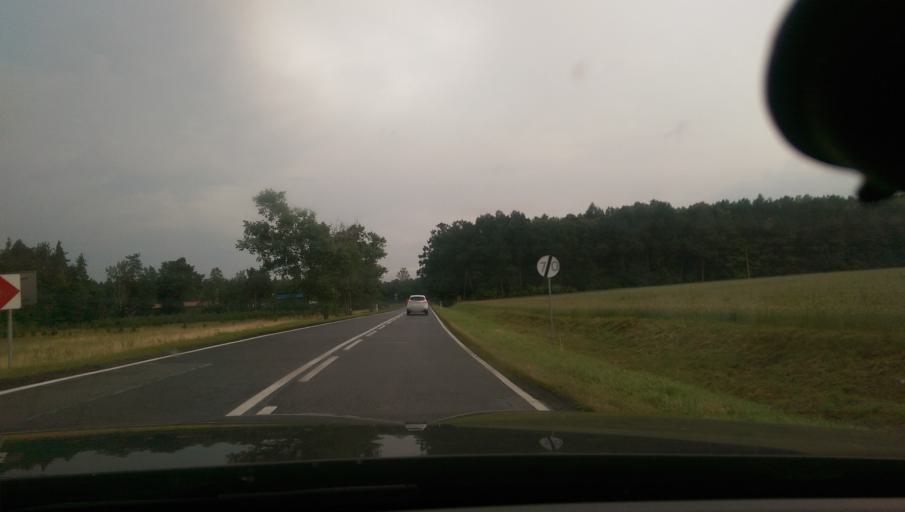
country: PL
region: Warmian-Masurian Voivodeship
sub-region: Powiat szczycienski
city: Szczytno
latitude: 53.5414
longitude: 20.9887
